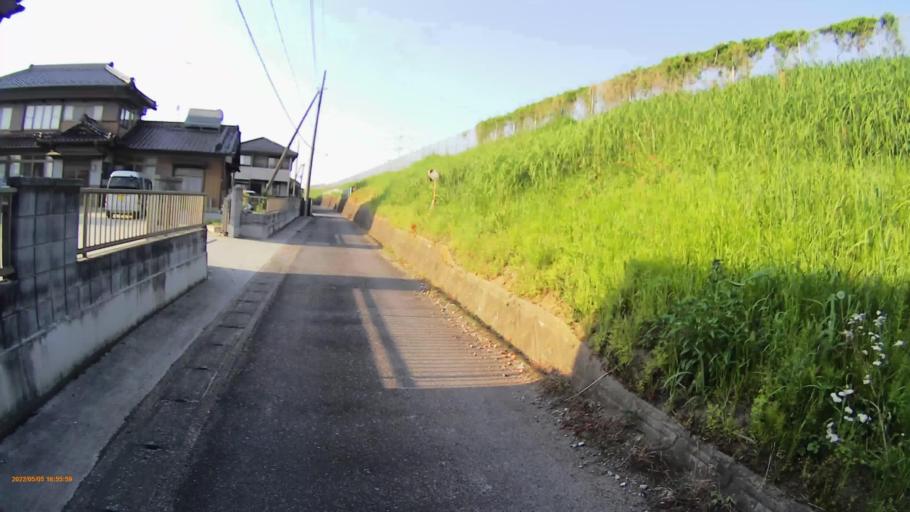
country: JP
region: Saitama
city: Kurihashi
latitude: 36.1097
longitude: 139.7237
